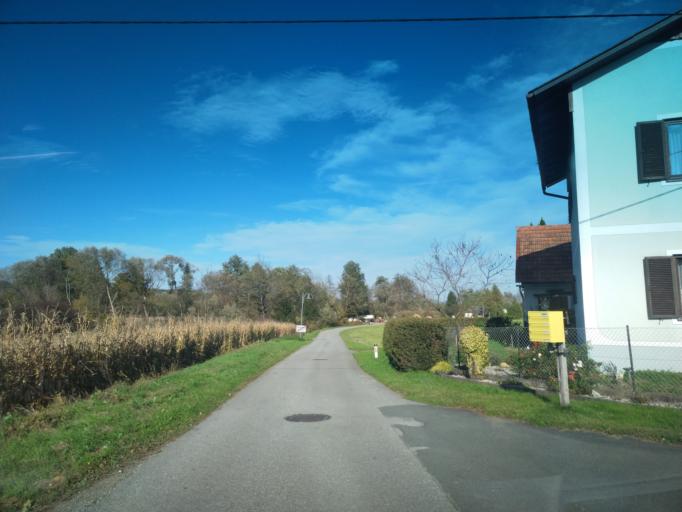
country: AT
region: Styria
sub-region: Politischer Bezirk Deutschlandsberg
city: Wies
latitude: 46.7224
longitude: 15.2990
